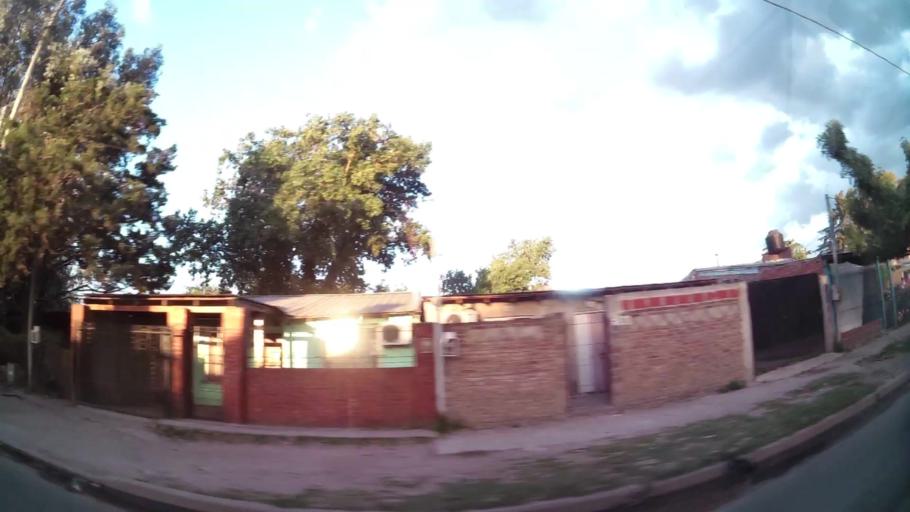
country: AR
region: Buenos Aires
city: Santa Catalina - Dique Lujan
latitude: -34.4849
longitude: -58.7499
